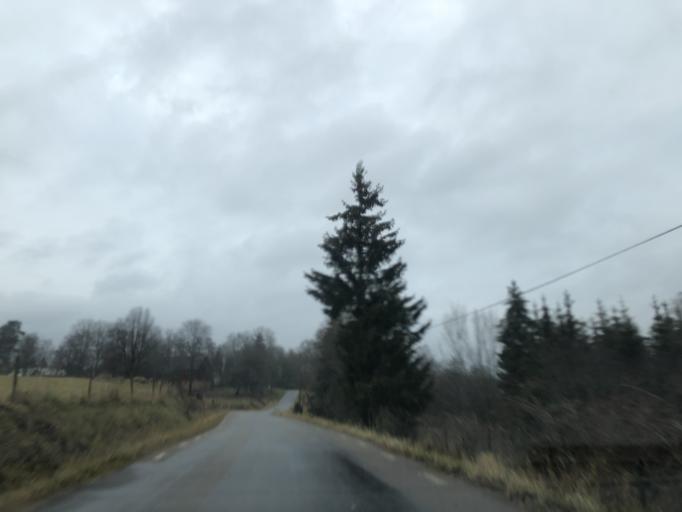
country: SE
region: Vaestra Goetaland
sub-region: Ulricehamns Kommun
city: Ulricehamn
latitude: 57.8790
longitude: 13.5206
